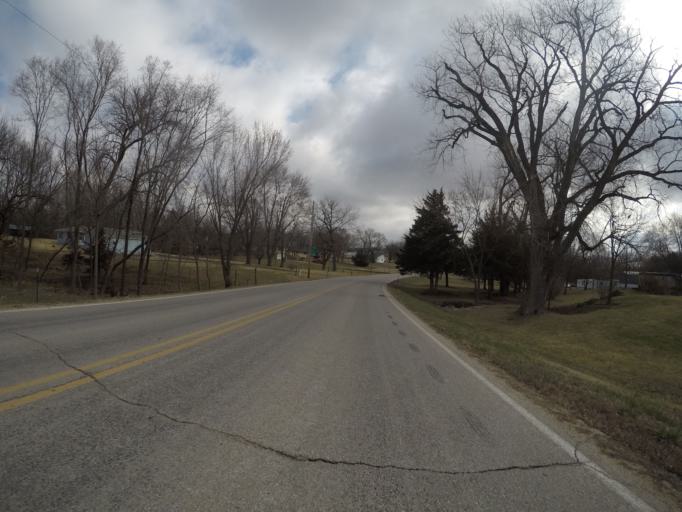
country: US
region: Kansas
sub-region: Pottawatomie County
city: Westmoreland
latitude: 39.3927
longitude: -96.4185
